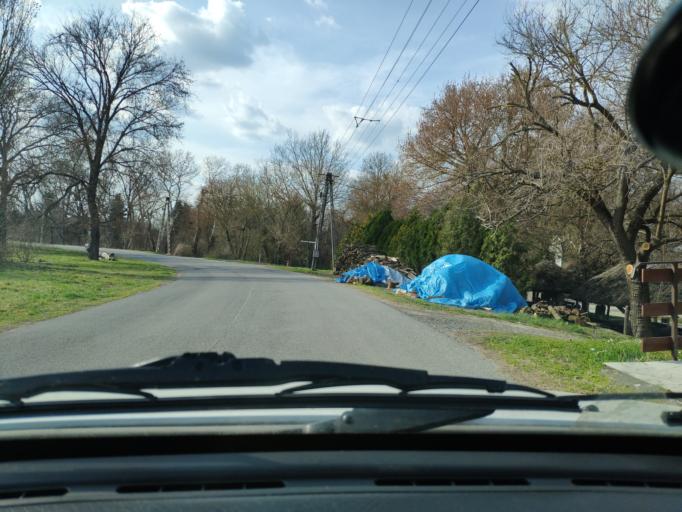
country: HU
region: Fejer
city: Adony
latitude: 47.1137
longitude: 18.8780
